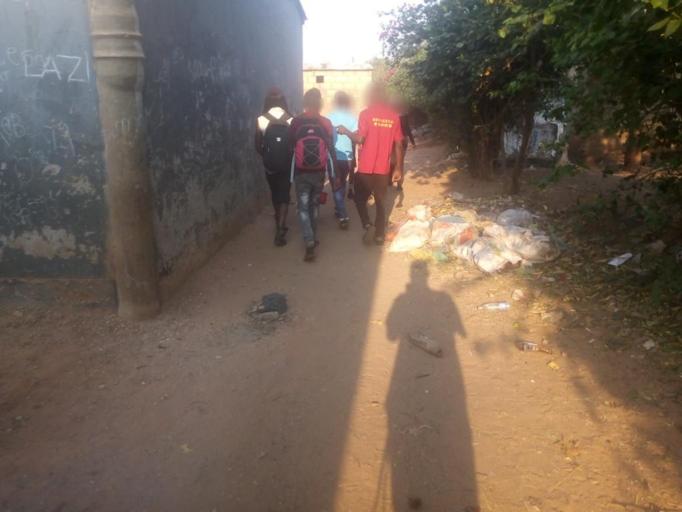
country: ZM
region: Lusaka
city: Lusaka
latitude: -15.4065
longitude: 28.3666
